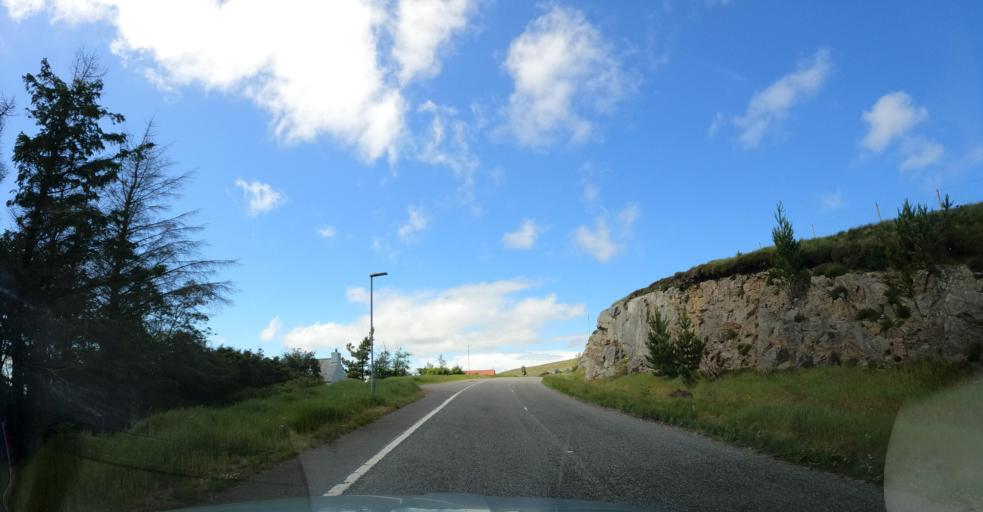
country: GB
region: Scotland
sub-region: Eilean Siar
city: Stornoway
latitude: 58.1687
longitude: -6.5661
